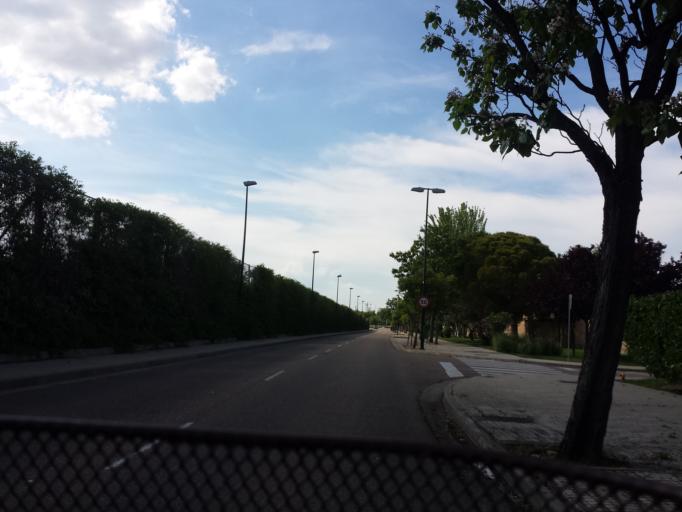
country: ES
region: Aragon
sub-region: Provincia de Zaragoza
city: Oliver-Valdefierro, Oliver, Valdefierro
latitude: 41.6317
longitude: -0.9204
